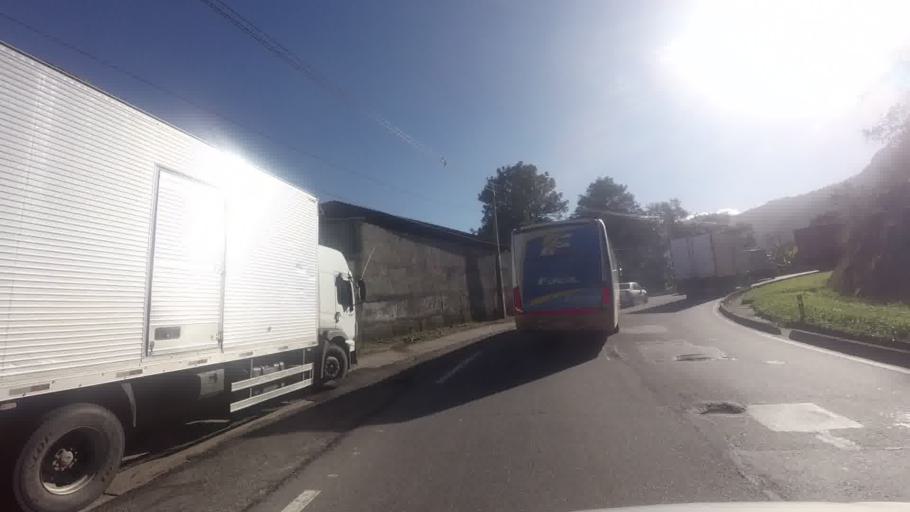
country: BR
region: Rio de Janeiro
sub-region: Petropolis
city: Petropolis
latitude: -22.5679
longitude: -43.2510
